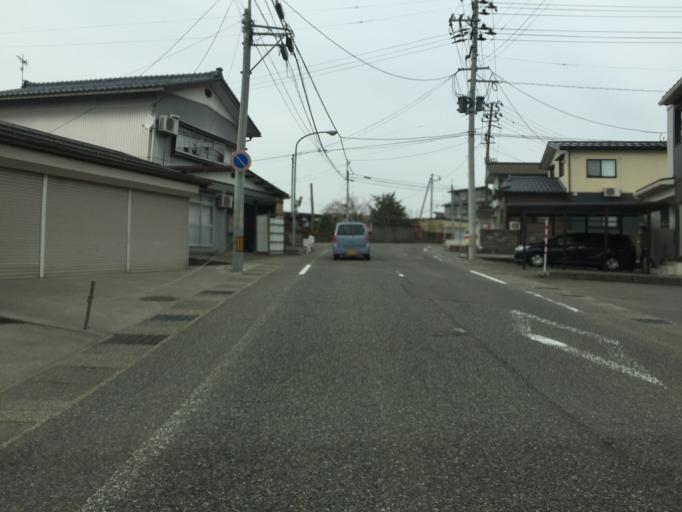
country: JP
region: Niigata
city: Tochio-honcho
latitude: 37.4794
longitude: 138.9972
